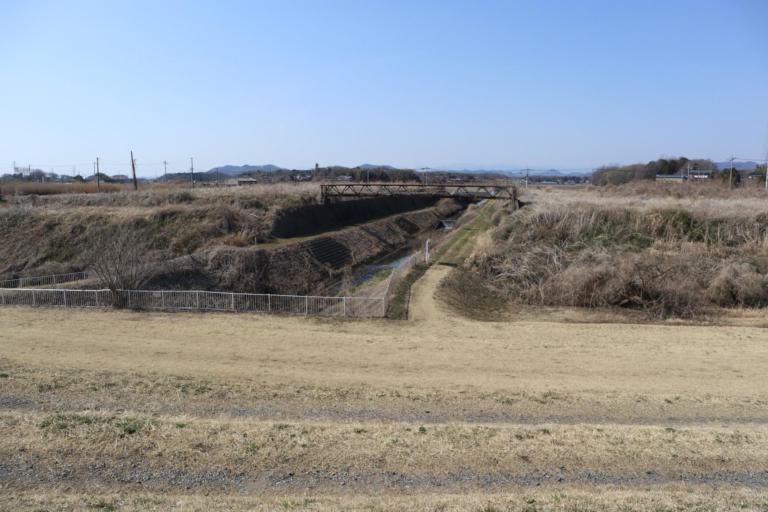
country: JP
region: Tochigi
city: Fujioka
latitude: 36.2764
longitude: 139.6844
